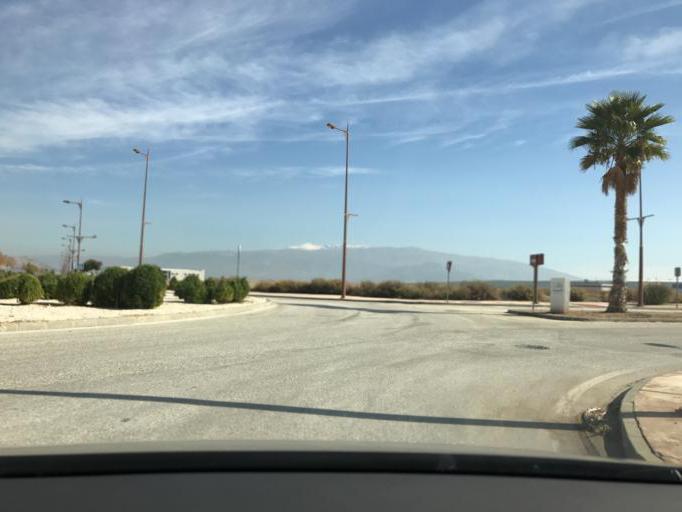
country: ES
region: Andalusia
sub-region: Provincia de Granada
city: Escuzar
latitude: 37.0808
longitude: -3.7625
